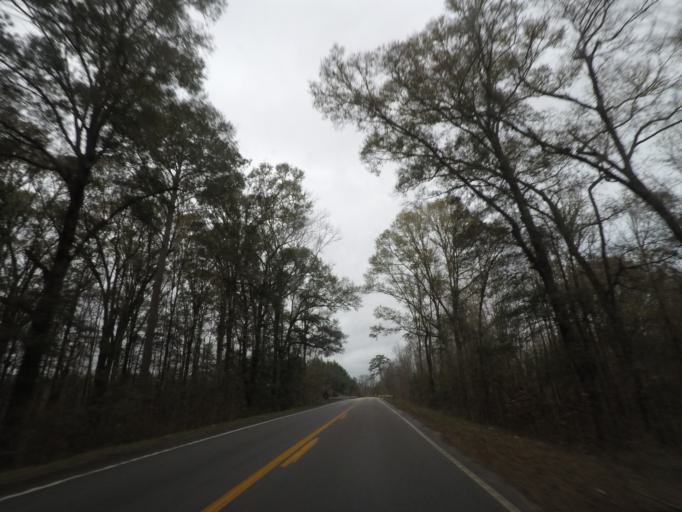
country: US
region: South Carolina
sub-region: Colleton County
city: Walterboro
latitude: 32.9134
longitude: -80.5280
